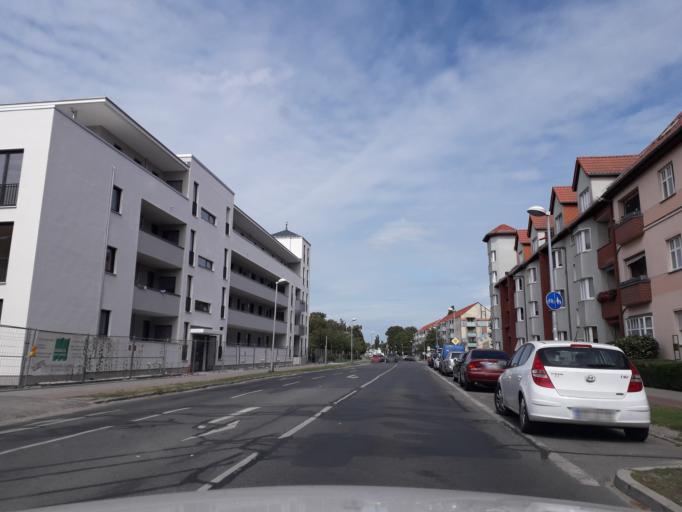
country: DE
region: Brandenburg
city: Hennigsdorf
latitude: 52.6416
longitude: 13.2006
